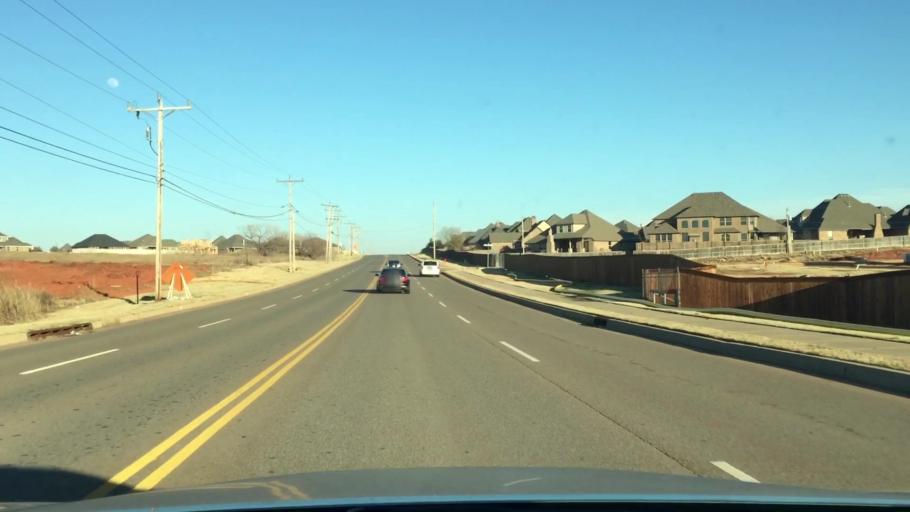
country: US
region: Oklahoma
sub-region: Oklahoma County
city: The Village
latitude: 35.6531
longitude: -97.5777
